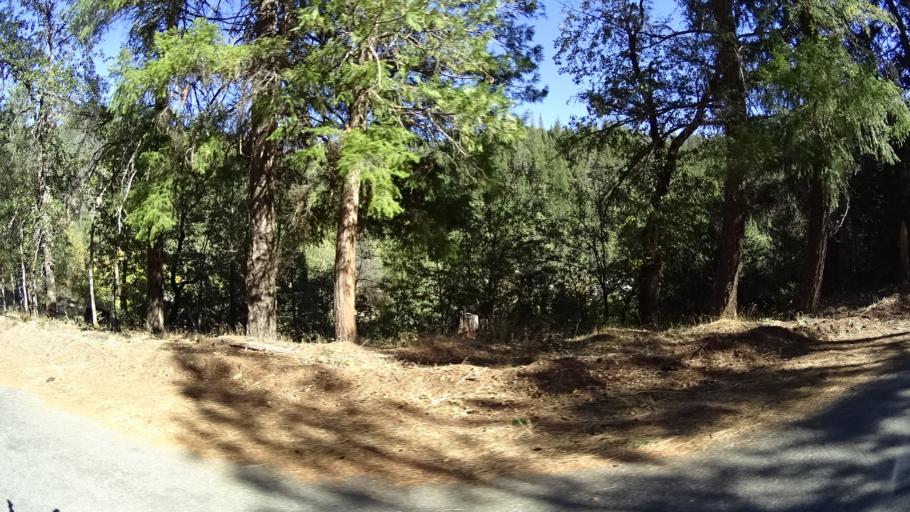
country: US
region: California
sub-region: Siskiyou County
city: Happy Camp
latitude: 41.3250
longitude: -123.0634
